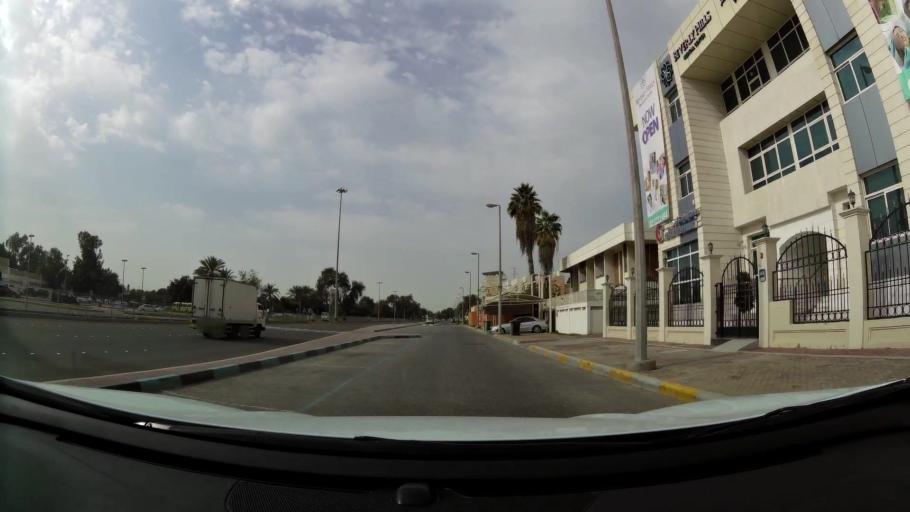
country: AE
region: Abu Dhabi
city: Abu Dhabi
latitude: 24.4570
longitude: 54.3809
